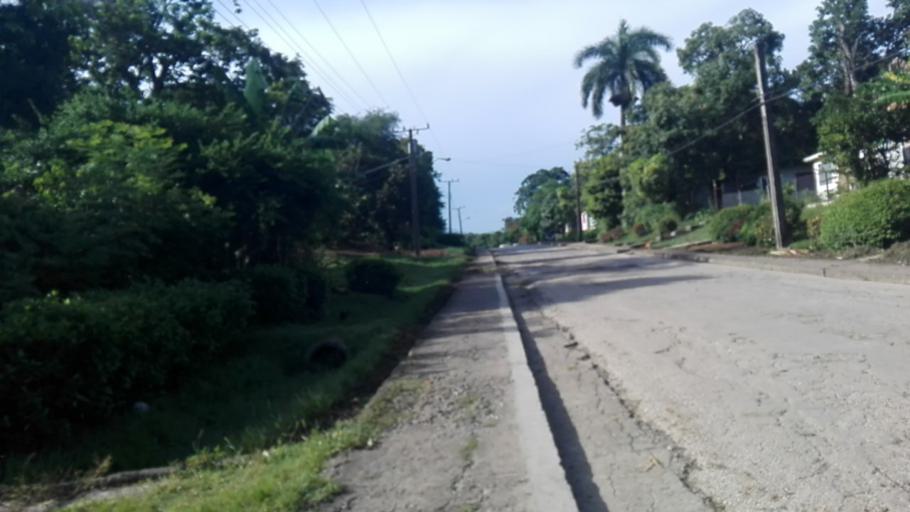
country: CU
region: Granma
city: Bartolome Maso
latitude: 20.1594
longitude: -76.9490
